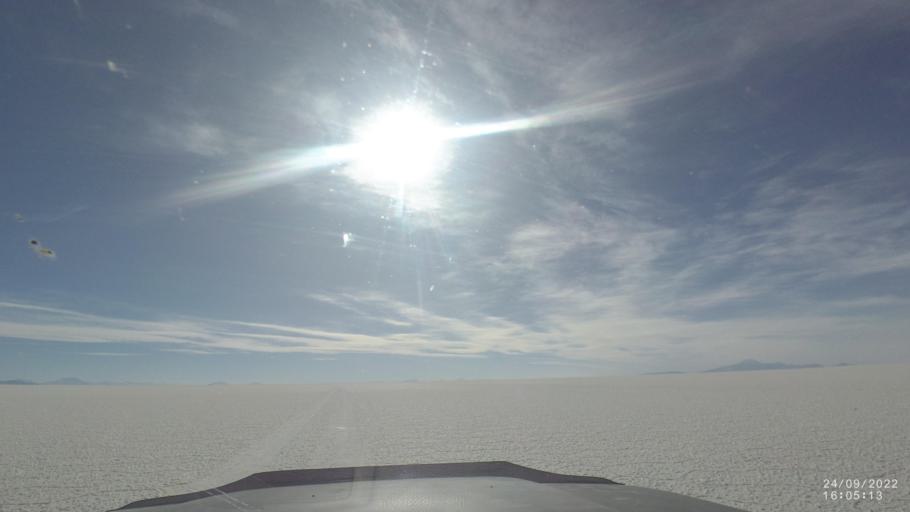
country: BO
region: Potosi
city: Colchani
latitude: -20.3112
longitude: -67.2893
